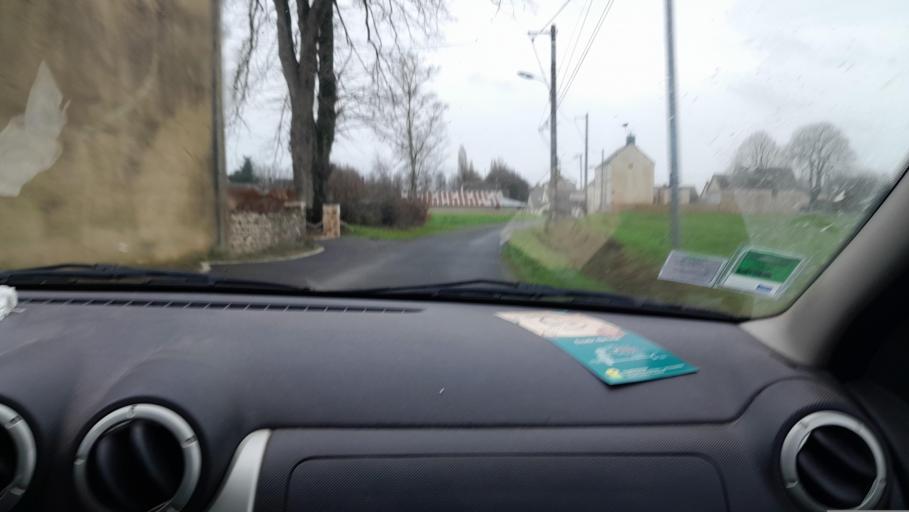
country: FR
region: Brittany
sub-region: Departement d'Ille-et-Vilaine
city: La Guerche-de-Bretagne
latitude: 47.9098
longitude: -1.1434
